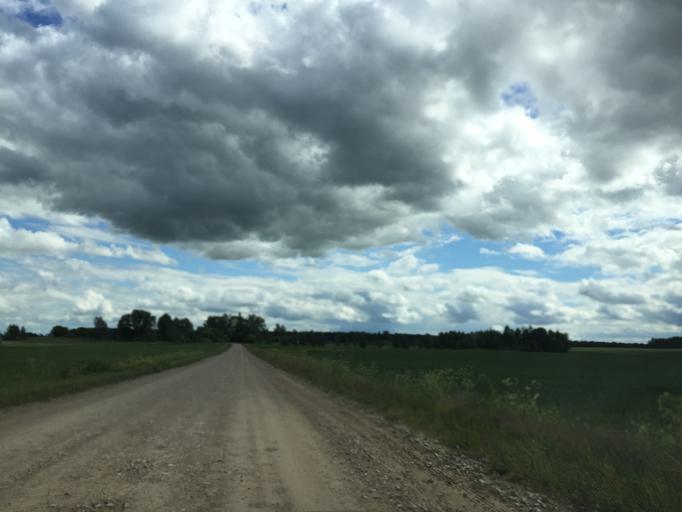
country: LV
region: Vecumnieki
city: Vecumnieki
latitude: 56.4763
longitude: 24.4179
